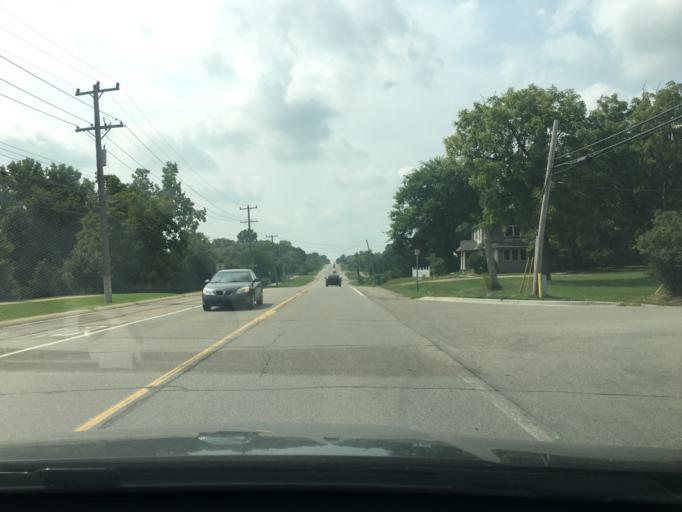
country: US
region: Michigan
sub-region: Oakland County
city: Rochester Hills
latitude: 42.6360
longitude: -83.1379
